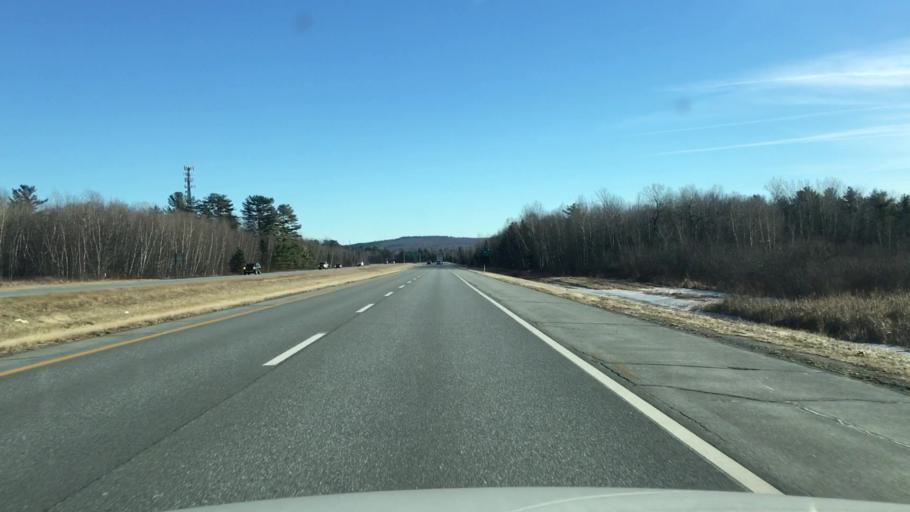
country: US
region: Maine
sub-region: Penobscot County
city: Brewer
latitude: 44.7723
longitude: -68.7431
